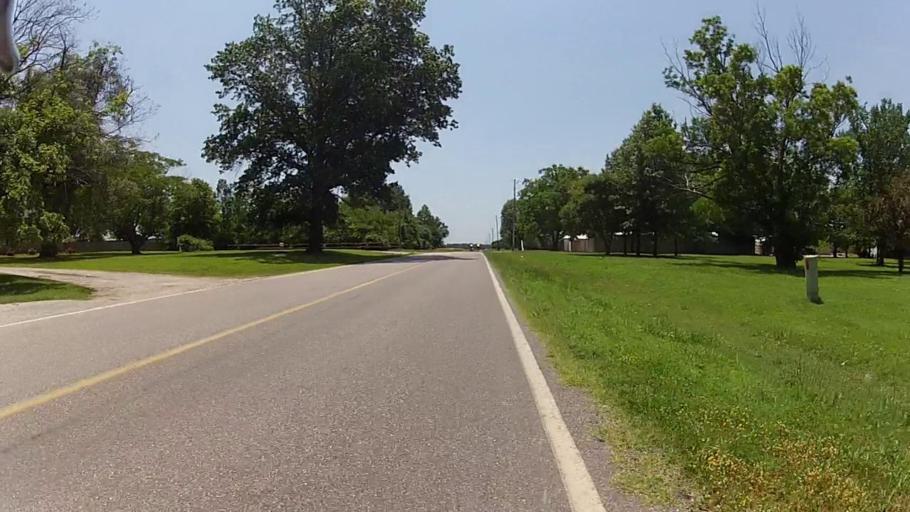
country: US
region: Kansas
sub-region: Montgomery County
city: Cherryvale
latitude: 37.2582
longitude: -95.5370
